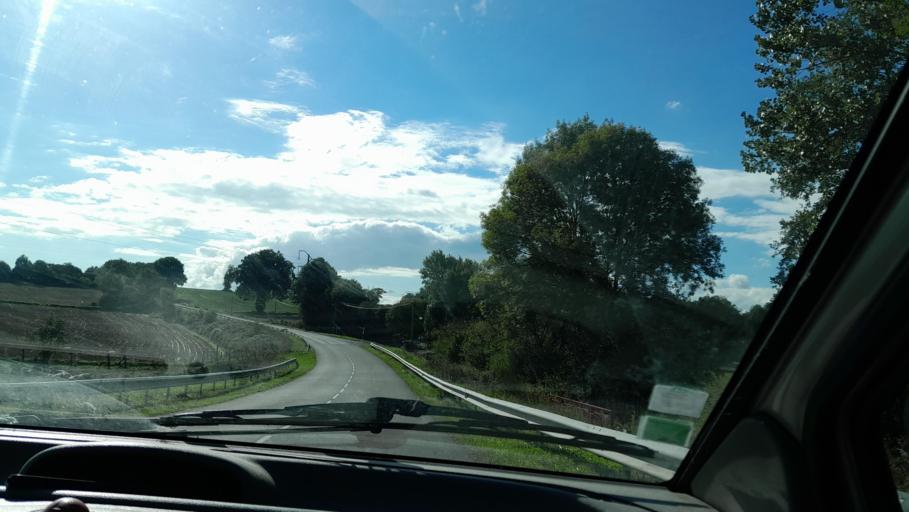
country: FR
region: Pays de la Loire
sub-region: Departement de la Mayenne
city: Ahuille
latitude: 48.0266
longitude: -0.8572
